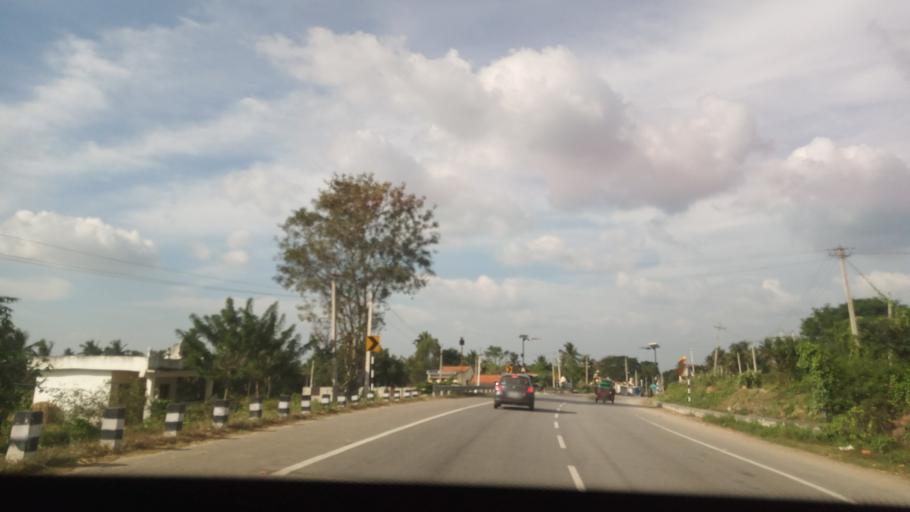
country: IN
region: Karnataka
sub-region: Mandya
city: Maddur
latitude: 12.6438
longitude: 77.0541
